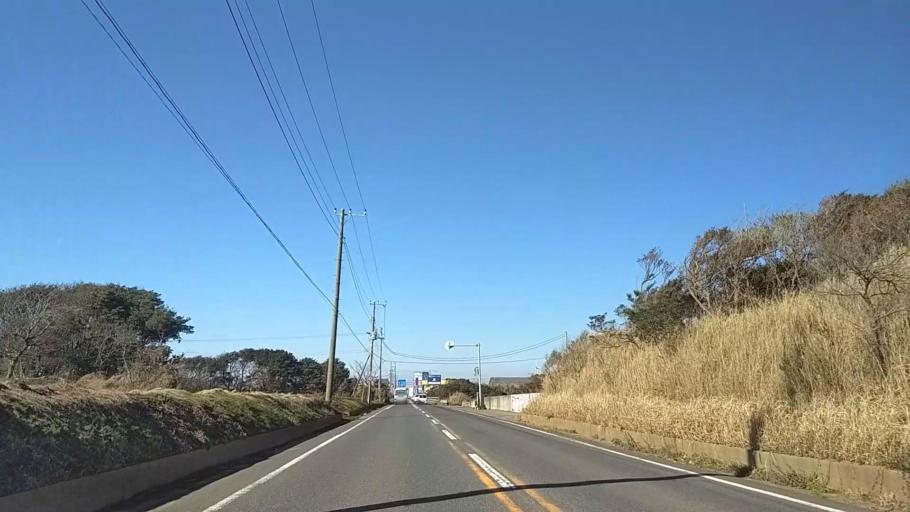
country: JP
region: Chiba
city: Hasaki
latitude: 35.7108
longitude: 140.7942
